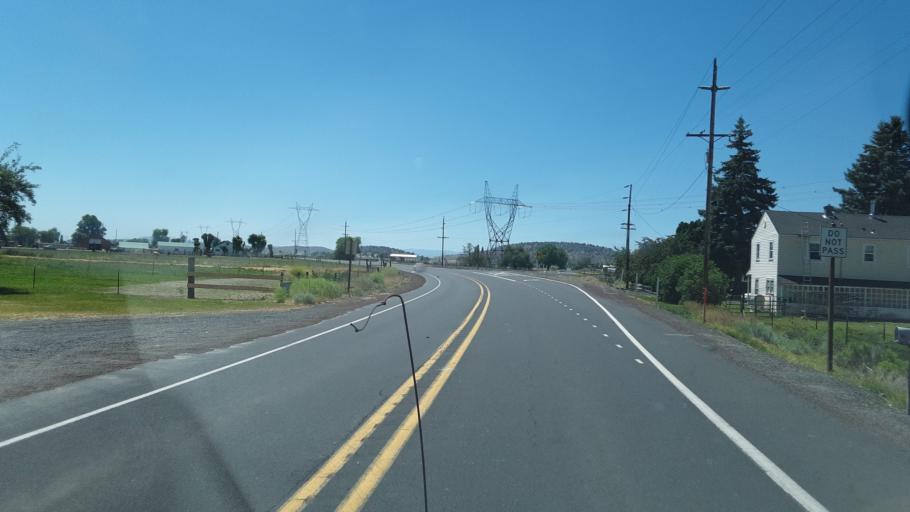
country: US
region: Oregon
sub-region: Klamath County
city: Altamont
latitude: 42.1054
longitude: -121.6985
